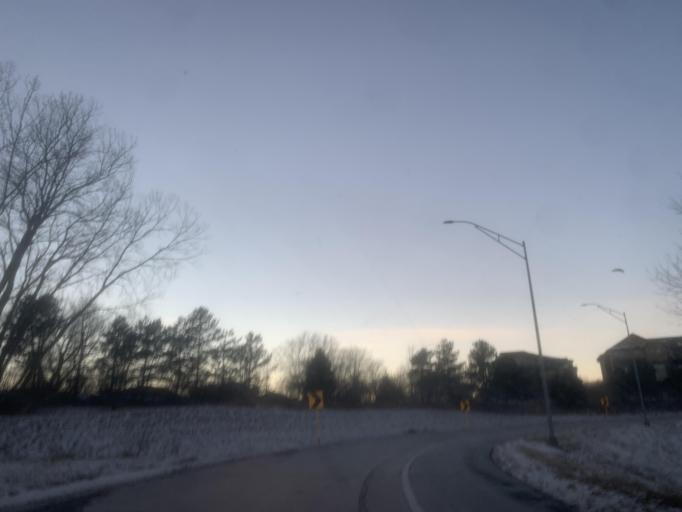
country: US
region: Nebraska
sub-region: Douglas County
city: Ralston
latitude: 41.2029
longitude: -96.0955
